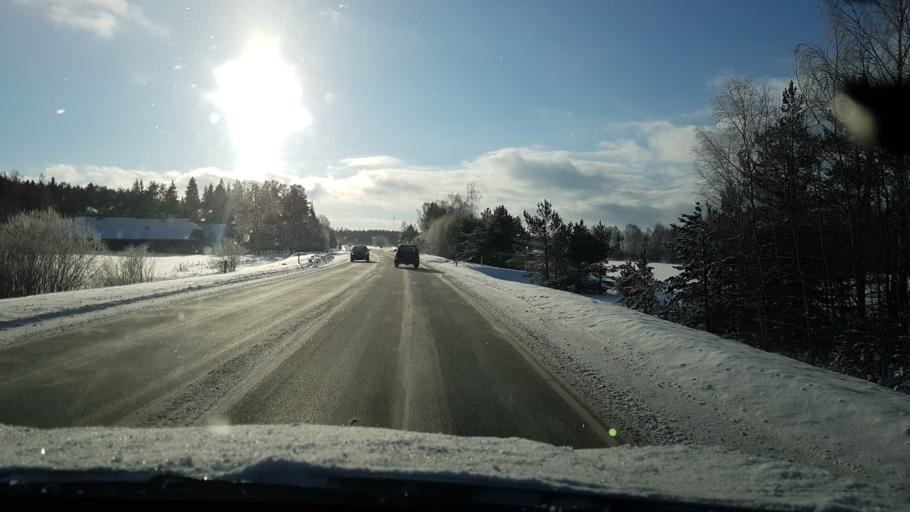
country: EE
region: Harju
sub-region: Nissi vald
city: Riisipere
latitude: 59.1406
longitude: 24.3306
